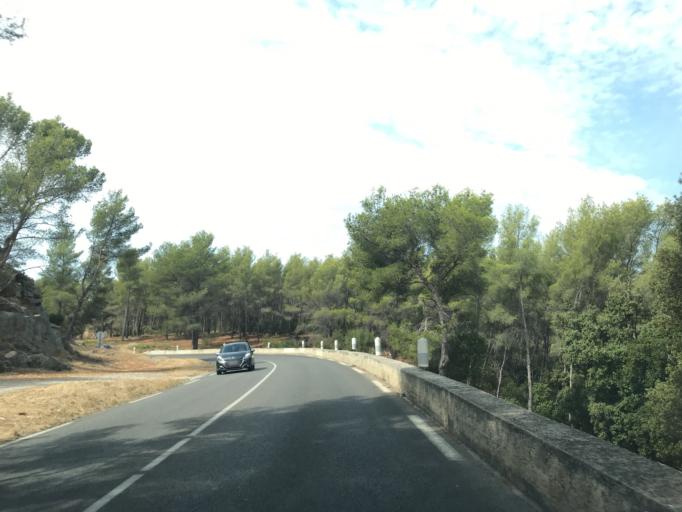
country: FR
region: Provence-Alpes-Cote d'Azur
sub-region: Departement du Var
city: Saint-Cyr-sur-Mer
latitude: 43.1682
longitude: 5.7180
